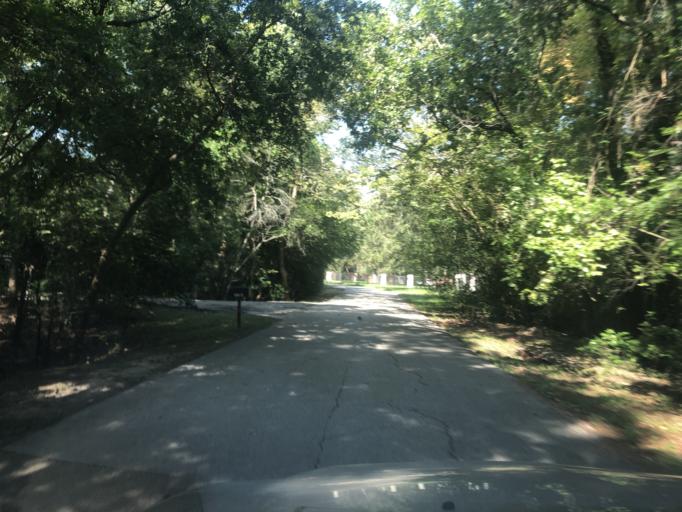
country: US
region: Texas
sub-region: Harris County
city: Bunker Hill Village
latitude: 29.7504
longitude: -95.5438
